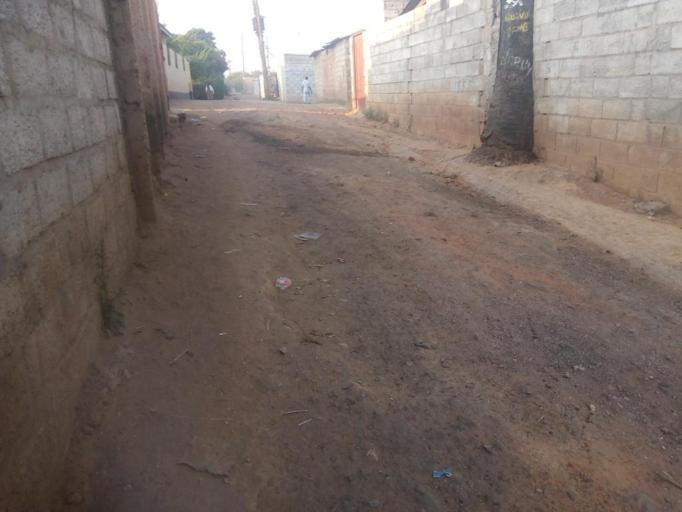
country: ZM
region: Lusaka
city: Lusaka
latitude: -15.4080
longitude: 28.3643
